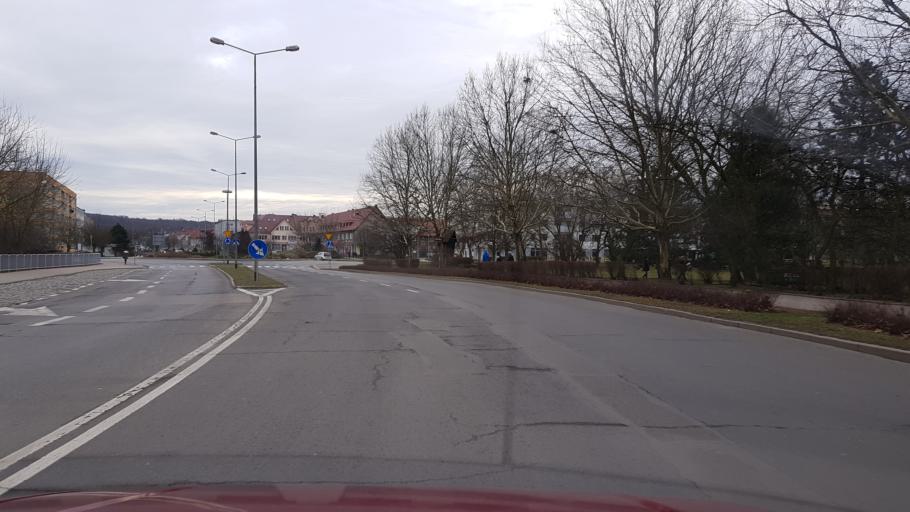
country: PL
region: West Pomeranian Voivodeship
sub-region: Powiat policki
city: Police
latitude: 53.5446
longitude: 14.5585
